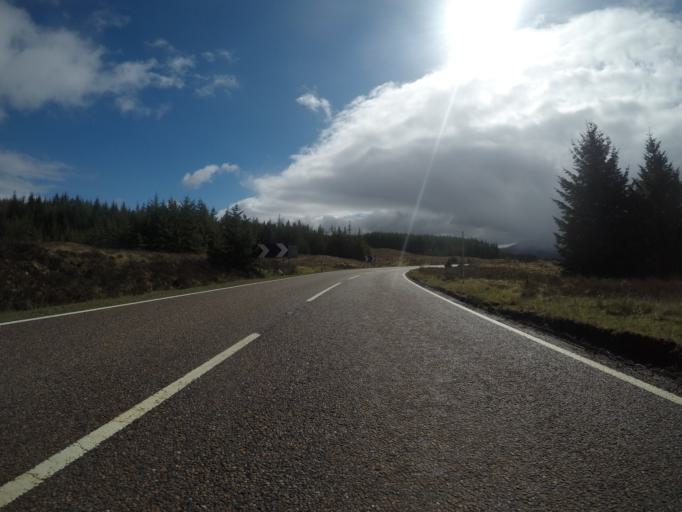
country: GB
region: Scotland
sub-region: Highland
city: Spean Bridge
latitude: 57.0933
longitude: -4.9879
